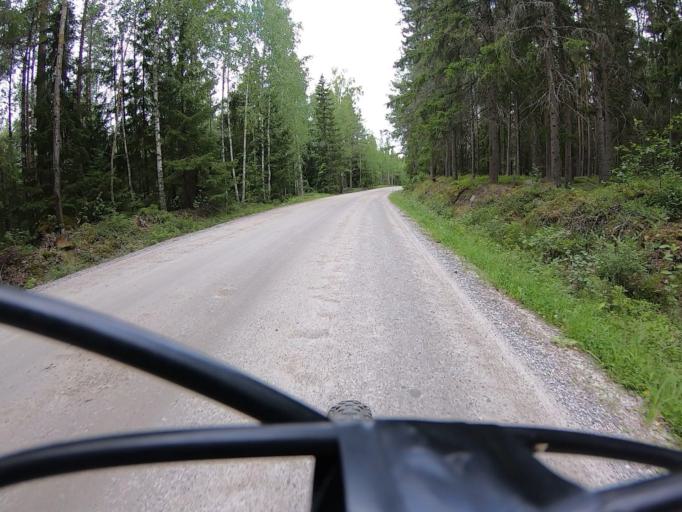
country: FI
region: Varsinais-Suomi
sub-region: Vakka-Suomi
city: Uusikaupunki
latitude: 60.8476
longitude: 21.3779
